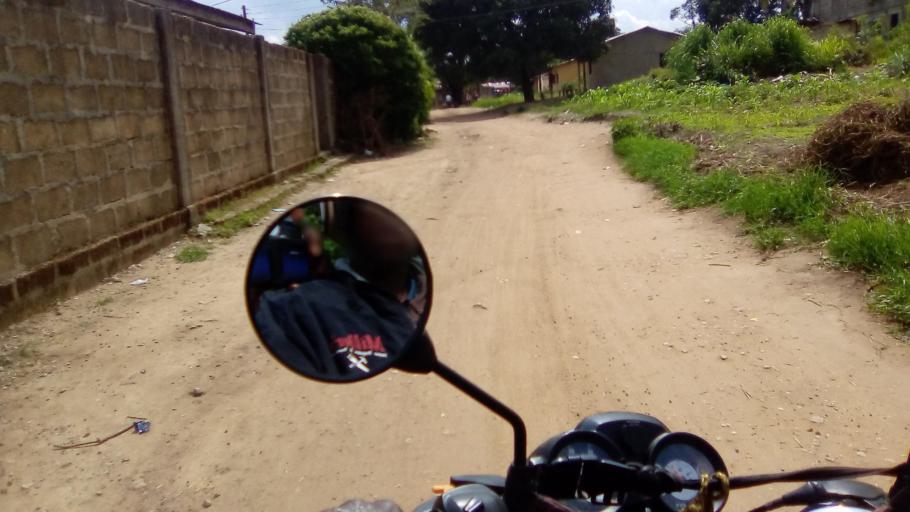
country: SL
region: Southern Province
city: Bo
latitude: 7.9488
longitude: -11.7233
